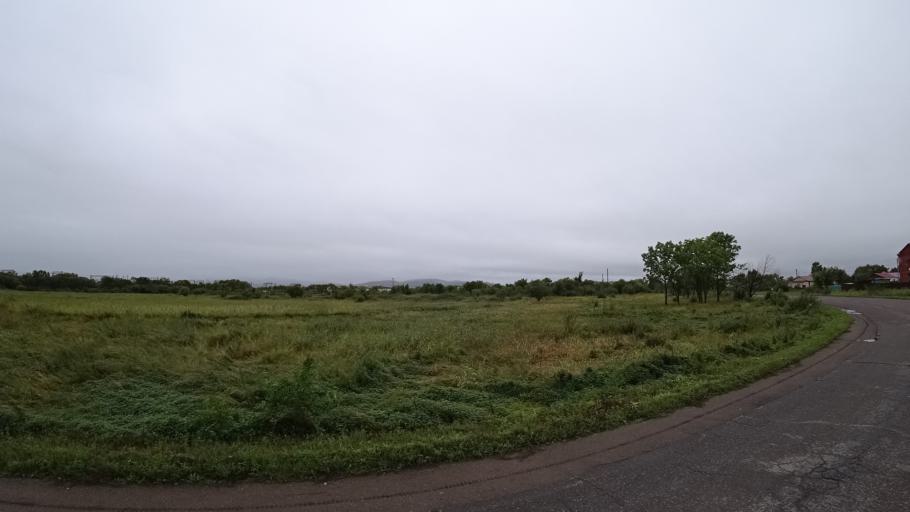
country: RU
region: Primorskiy
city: Monastyrishche
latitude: 44.2035
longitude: 132.4324
